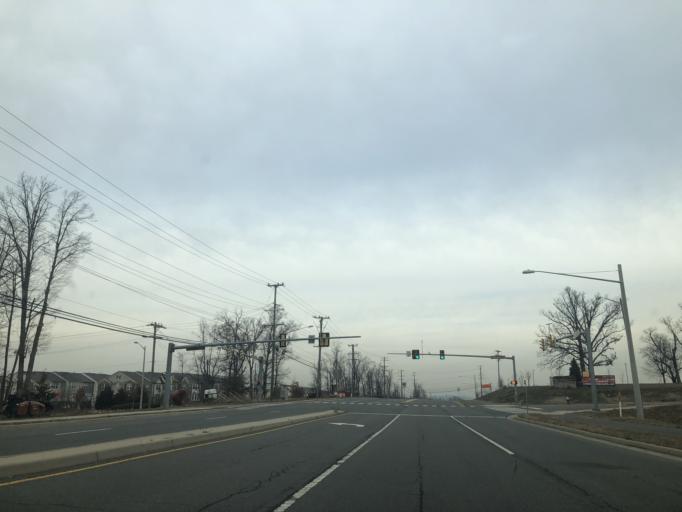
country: US
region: Virginia
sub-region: Loudoun County
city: Leesburg
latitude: 39.0863
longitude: -77.5530
